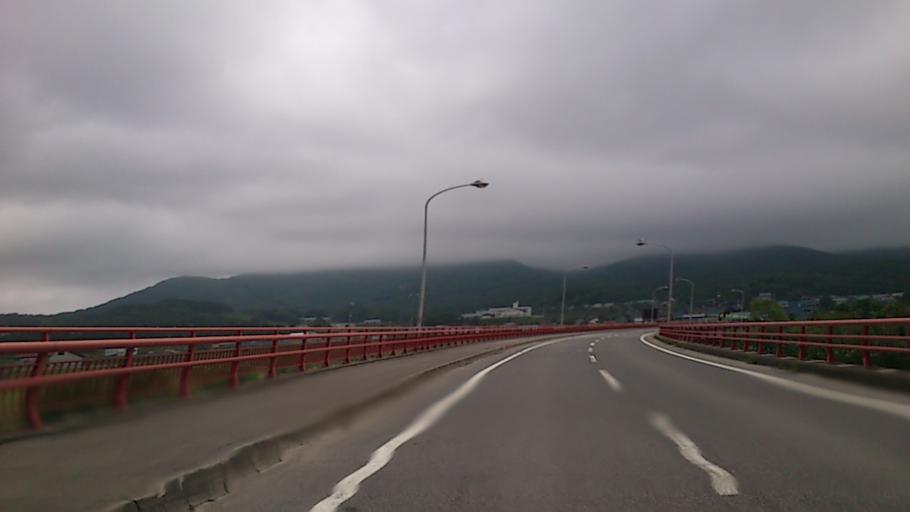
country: JP
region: Hokkaido
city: Niseko Town
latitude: 42.8164
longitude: 140.5262
